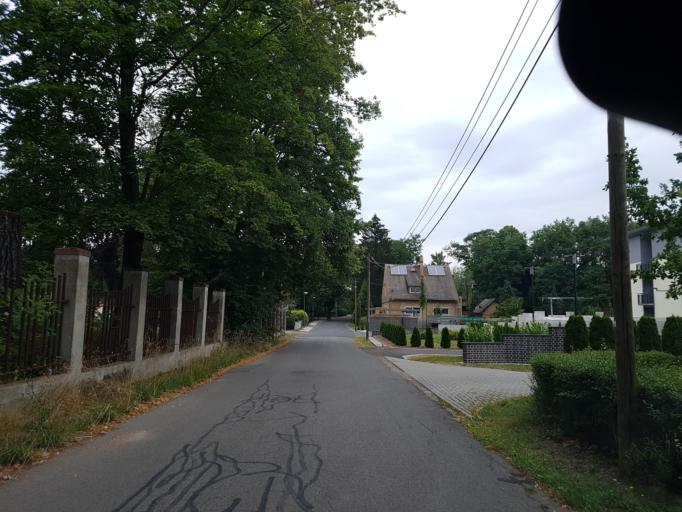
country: DE
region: Brandenburg
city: Sallgast
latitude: 51.5620
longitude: 13.8849
